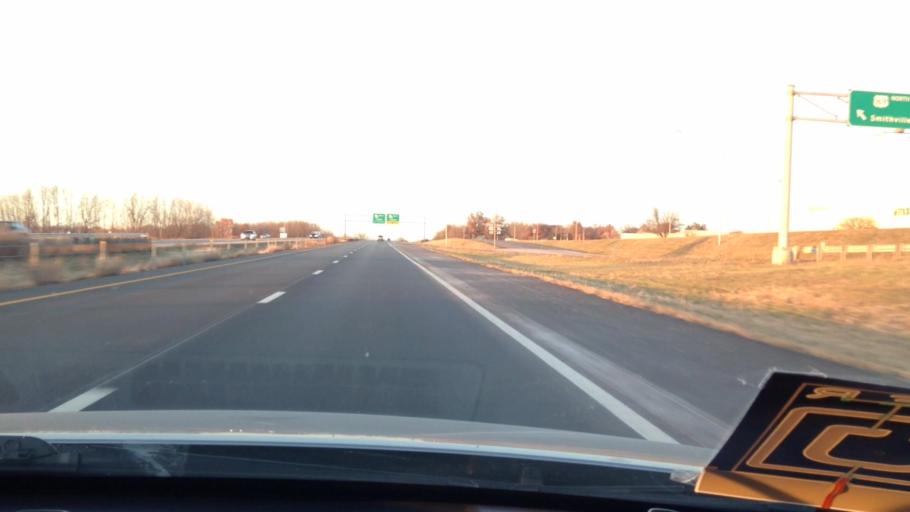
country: US
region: Missouri
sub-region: Clay County
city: Gladstone
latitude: 39.2471
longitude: -94.5902
